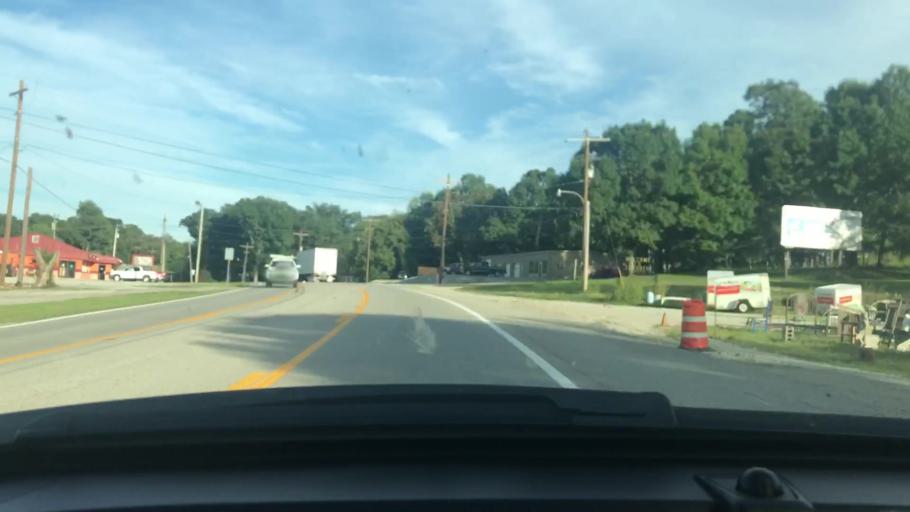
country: US
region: Arkansas
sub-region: Randolph County
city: Pocahontas
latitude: 36.2044
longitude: -91.1917
